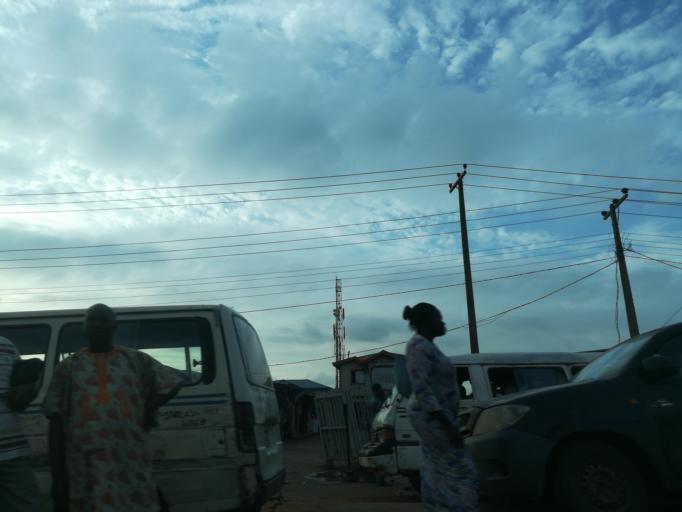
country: NG
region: Lagos
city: Ojota
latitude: 6.6103
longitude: 3.4108
